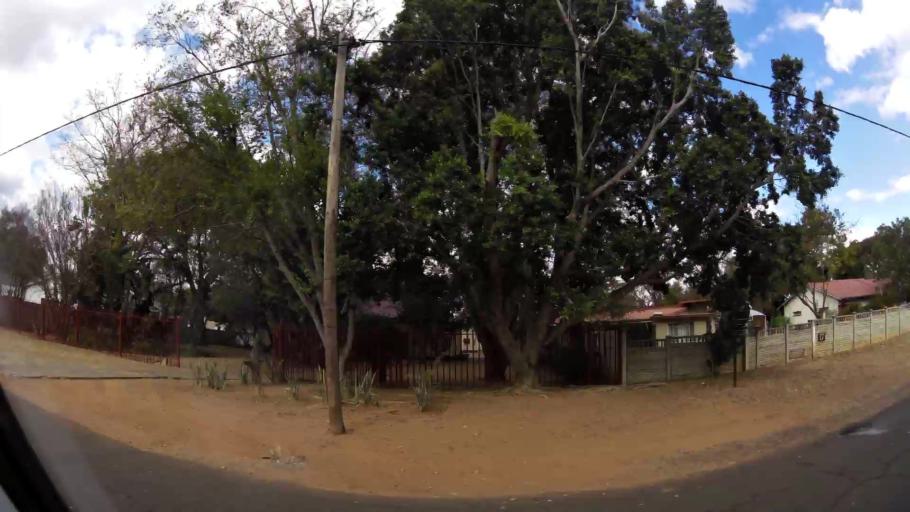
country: ZA
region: Limpopo
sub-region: Waterberg District Municipality
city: Modimolle
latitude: -24.7068
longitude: 28.4033
